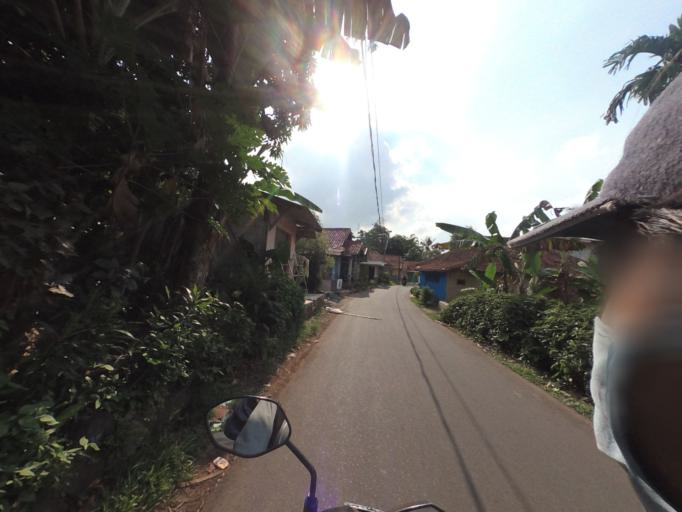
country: ID
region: West Java
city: Ciampea
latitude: -6.6068
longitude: 106.7063
